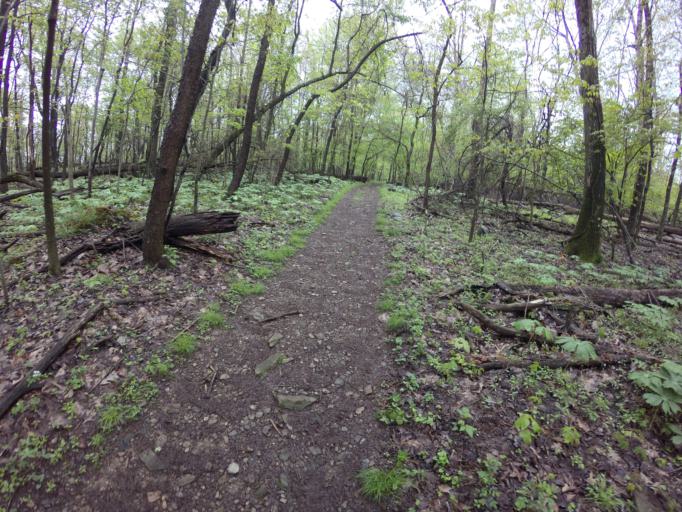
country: US
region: Maryland
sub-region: Washington County
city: Boonsboro
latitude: 39.5149
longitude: -77.6192
